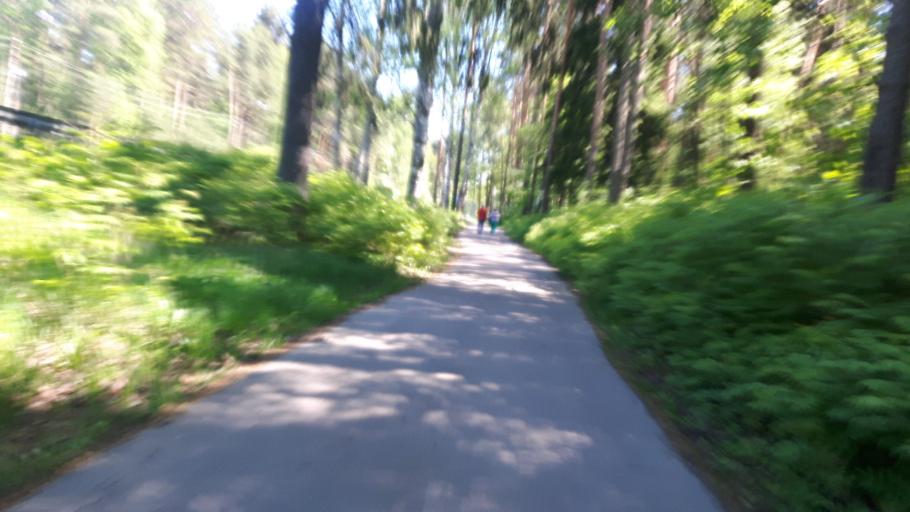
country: RU
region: St.-Petersburg
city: Zelenogorsk
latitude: 60.1923
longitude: 29.6796
